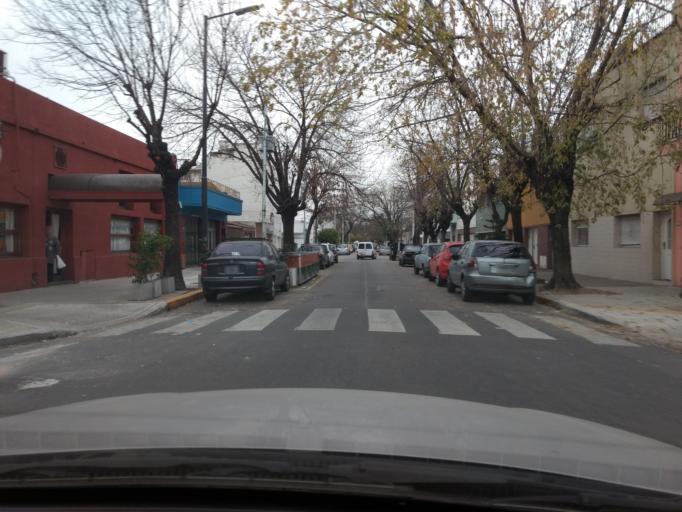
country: AR
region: Buenos Aires F.D.
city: Villa Santa Rita
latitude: -34.6251
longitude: -58.5127
